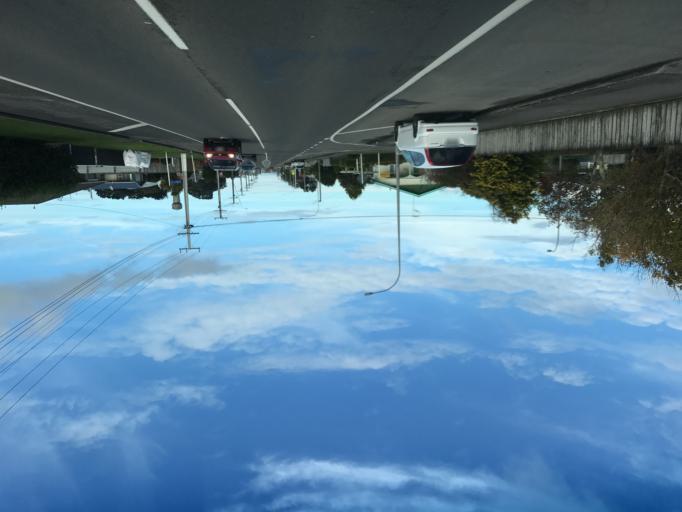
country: NZ
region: Manawatu-Wanganui
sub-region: Horowhenua District
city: Foxton
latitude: -40.4734
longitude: 175.2856
